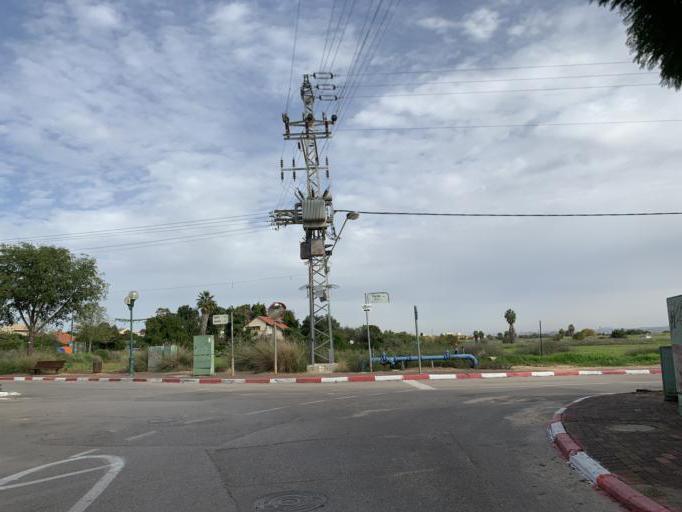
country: IL
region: Central District
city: Hod HaSharon
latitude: 32.1544
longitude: 34.9044
